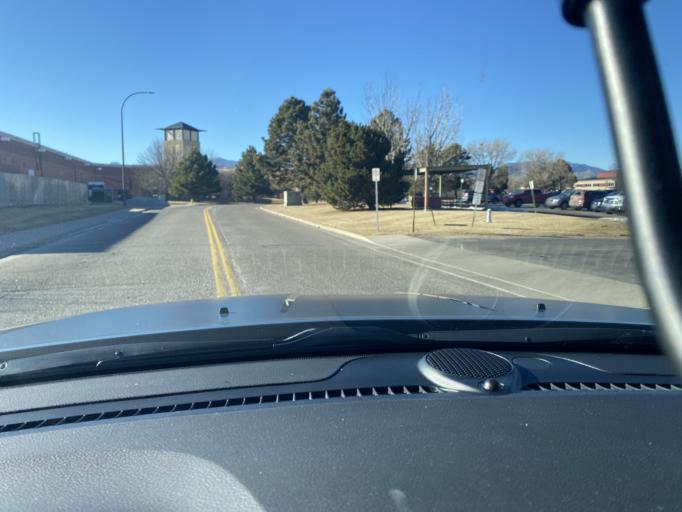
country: US
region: Colorado
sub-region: Jefferson County
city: Applewood
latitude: 39.8141
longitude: -105.1606
